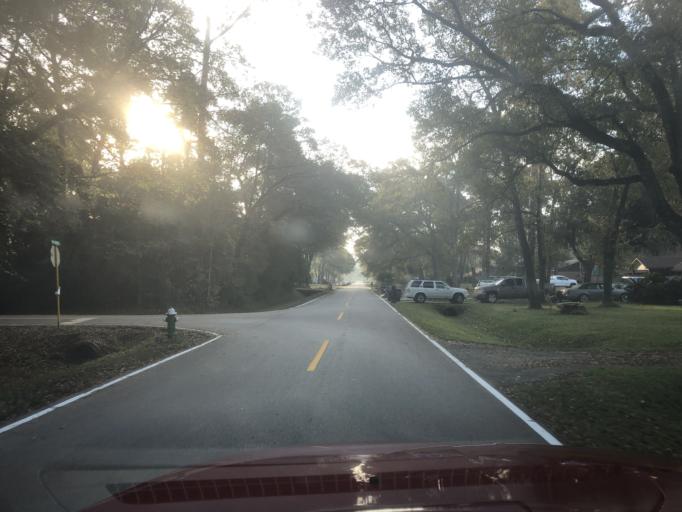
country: US
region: Texas
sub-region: Harris County
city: Spring
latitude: 30.0192
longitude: -95.4783
